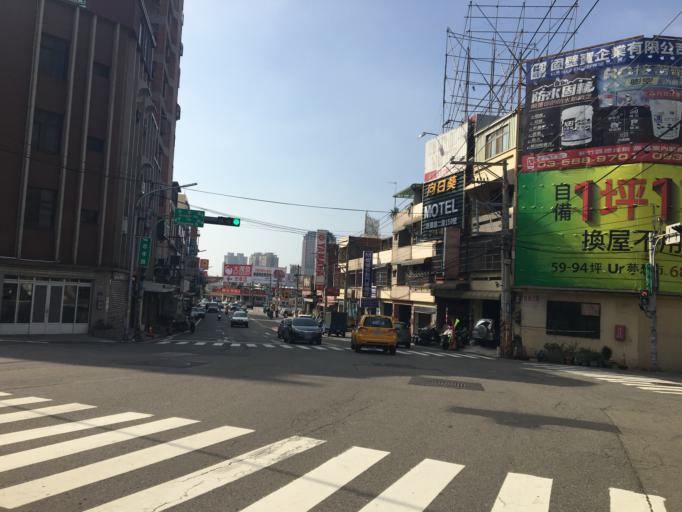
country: TW
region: Taiwan
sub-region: Hsinchu
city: Hsinchu
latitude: 24.8057
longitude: 120.9885
